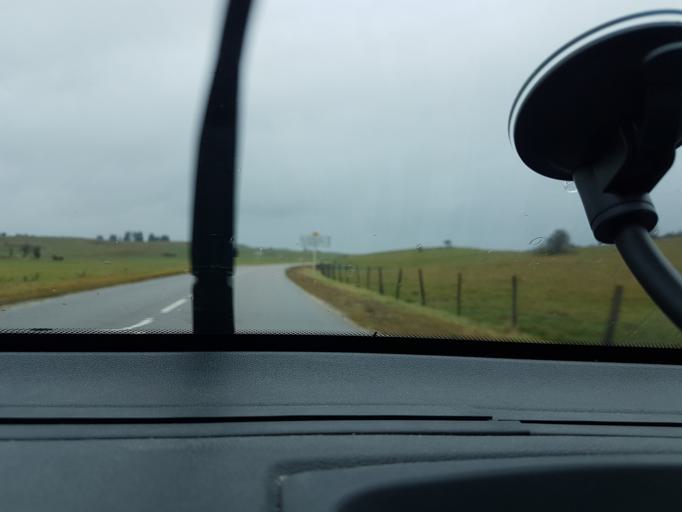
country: FR
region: Franche-Comte
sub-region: Departement du Doubs
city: Vercel-Villedieu-le-Camp
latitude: 47.1467
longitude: 6.4459
